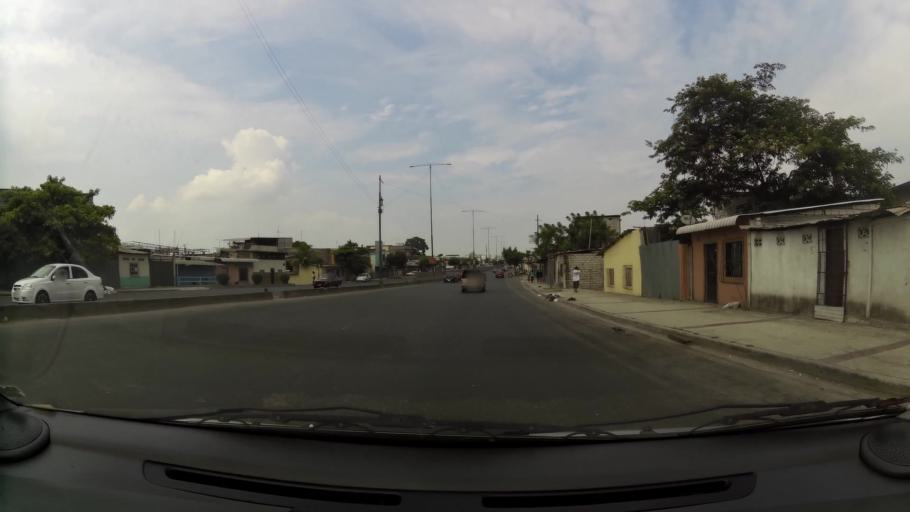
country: EC
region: Guayas
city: Guayaquil
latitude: -2.2391
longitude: -79.9112
